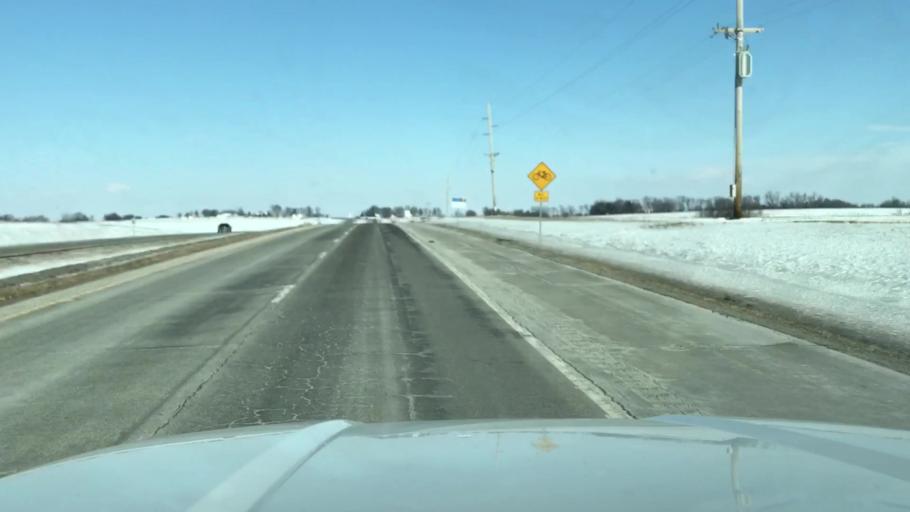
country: US
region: Missouri
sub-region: Nodaway County
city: Maryville
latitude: 40.2591
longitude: -94.8668
